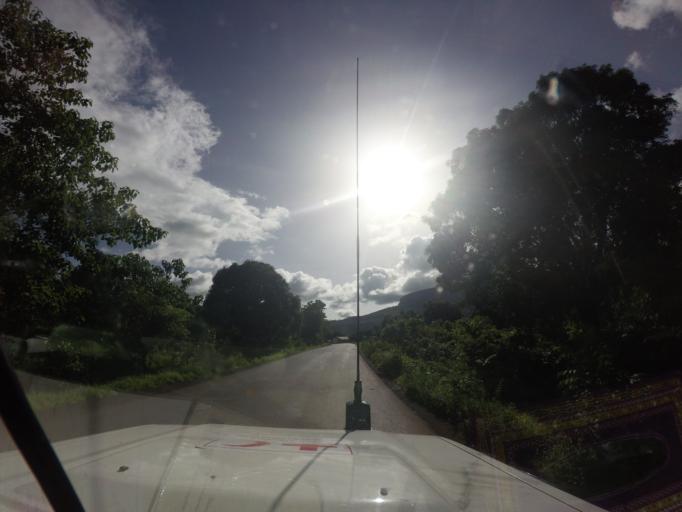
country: GN
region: Kindia
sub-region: Kindia
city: Kindia
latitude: 10.1800
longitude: -12.4923
